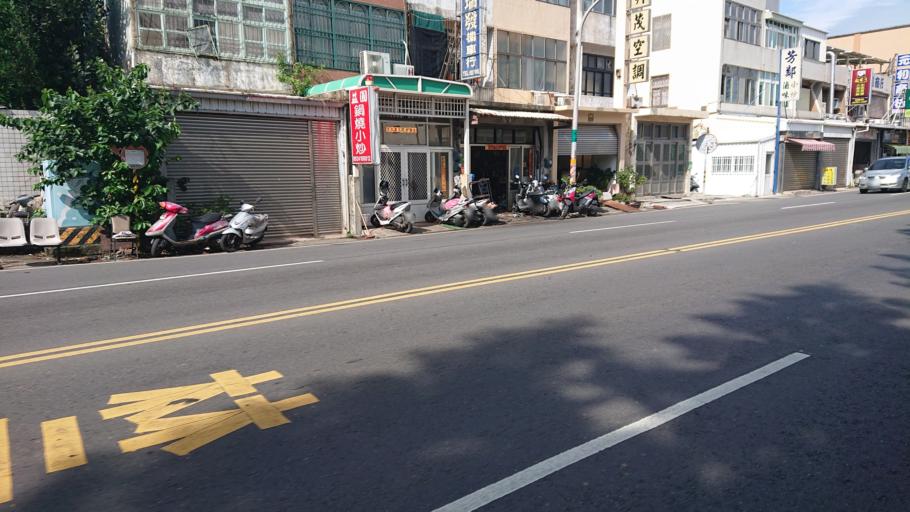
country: TW
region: Taiwan
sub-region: Penghu
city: Ma-kung
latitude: 23.5598
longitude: 119.5973
